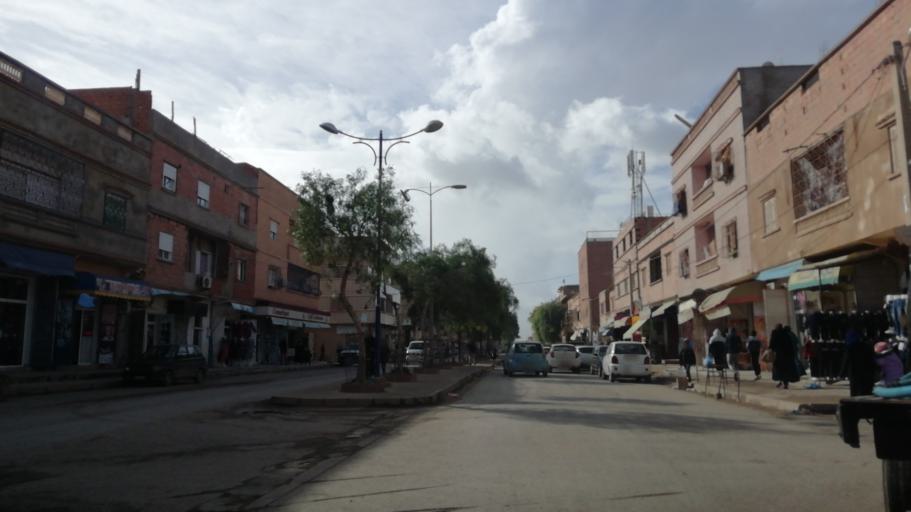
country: DZ
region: Oran
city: Es Senia
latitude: 35.6428
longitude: -0.5732
